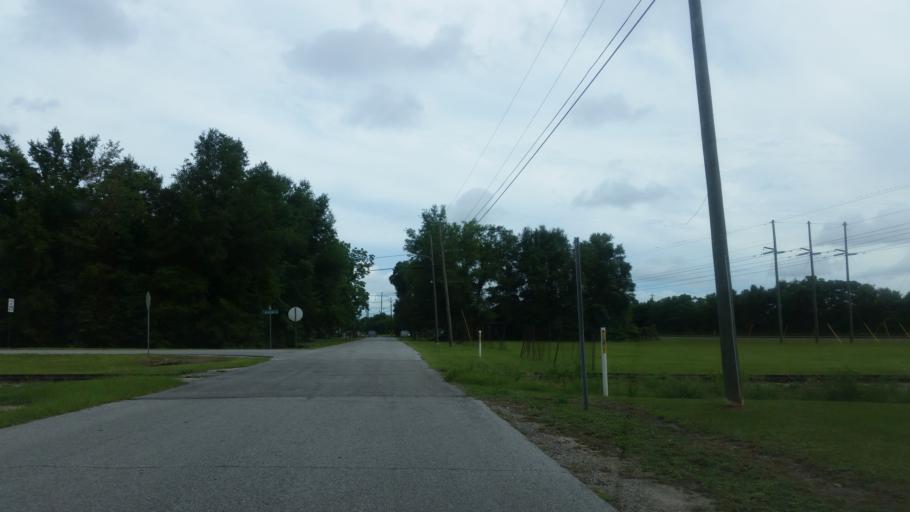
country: US
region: Florida
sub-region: Escambia County
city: Goulding
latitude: 30.4445
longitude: -87.2226
